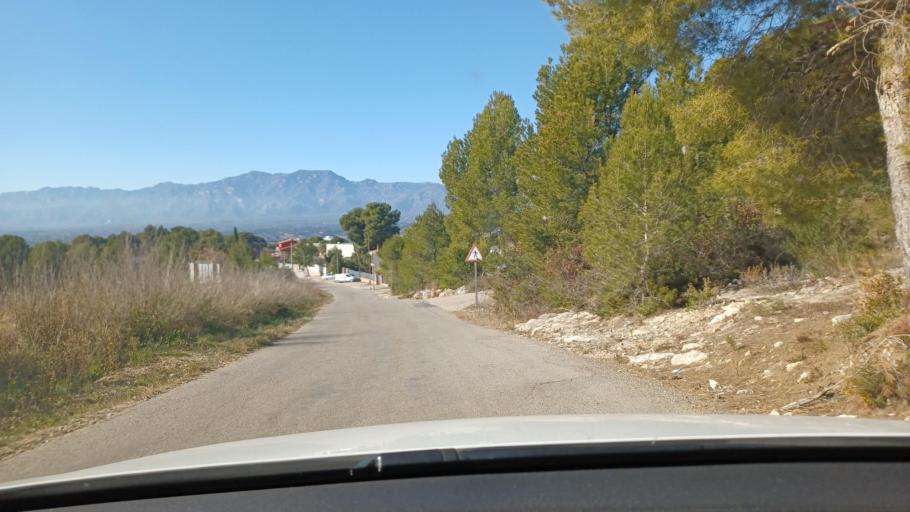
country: ES
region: Catalonia
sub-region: Provincia de Tarragona
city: Tortosa
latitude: 40.8139
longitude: 0.5487
